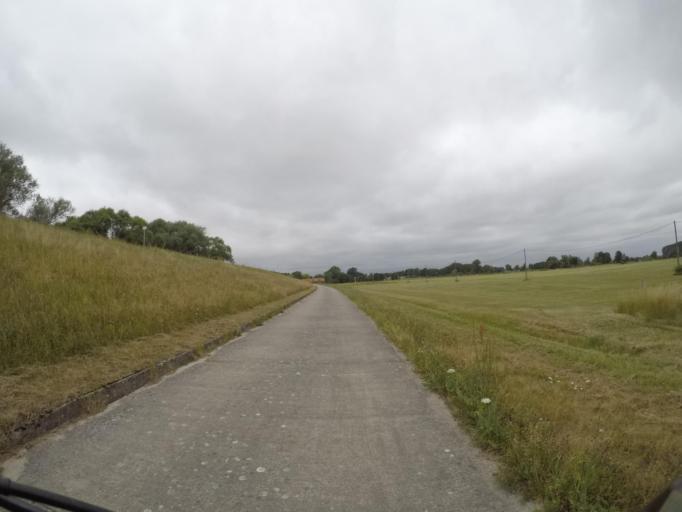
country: DE
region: Lower Saxony
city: Hitzacker
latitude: 53.1507
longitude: 11.0795
